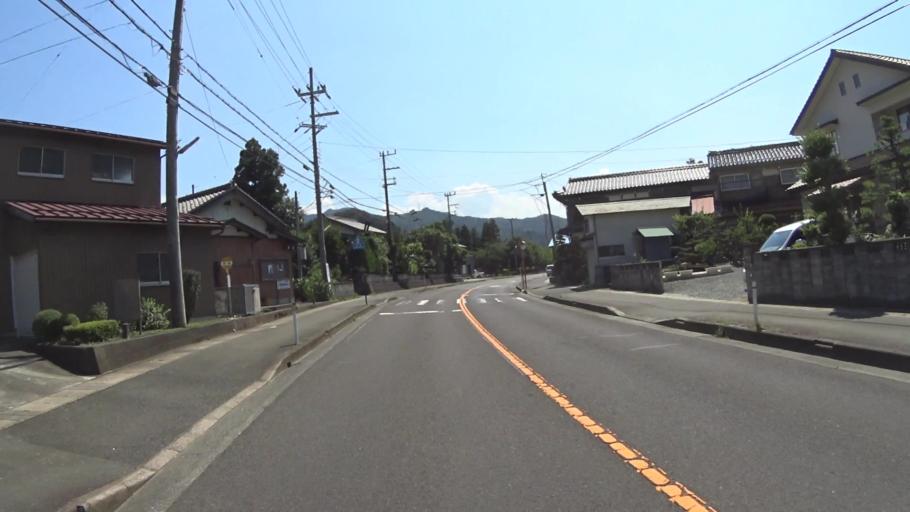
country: JP
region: Fukui
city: Obama
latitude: 35.4617
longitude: 135.7258
